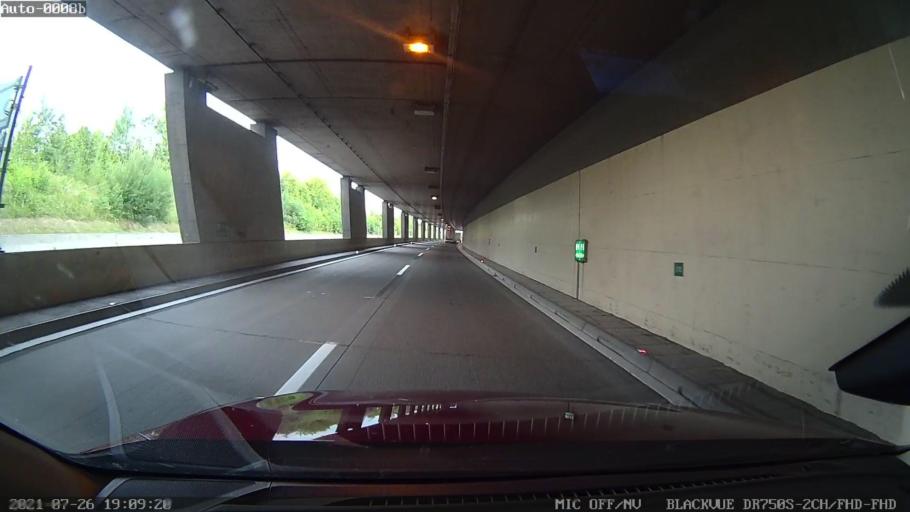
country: AT
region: Upper Austria
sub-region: Wels-Land
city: Steinhaus
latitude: 48.0994
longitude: 14.0201
